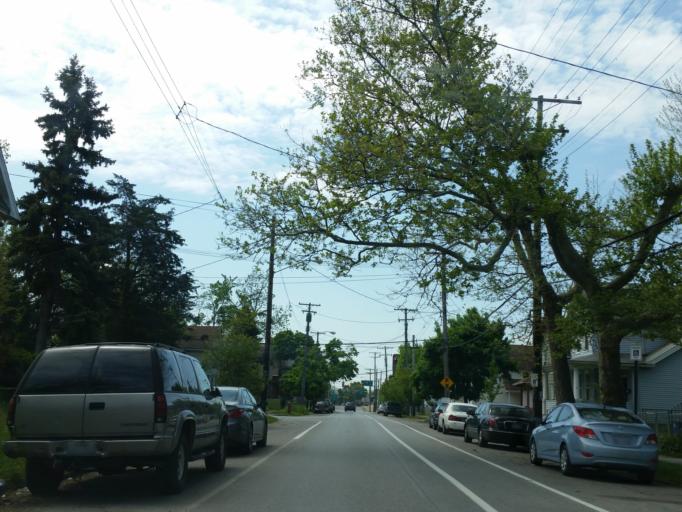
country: US
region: Ohio
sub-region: Cuyahoga County
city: Cleveland
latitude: 41.4782
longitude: -81.7165
